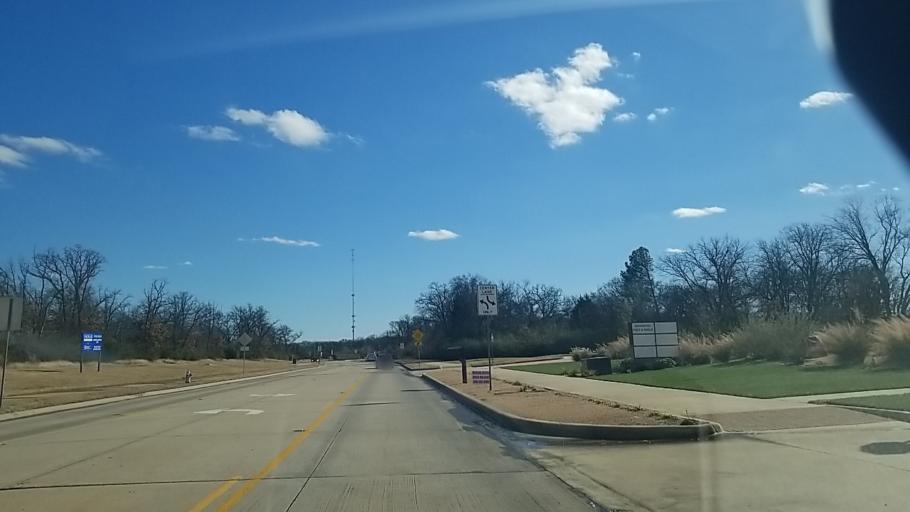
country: US
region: Texas
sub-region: Denton County
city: Corinth
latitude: 33.1838
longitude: -97.0955
